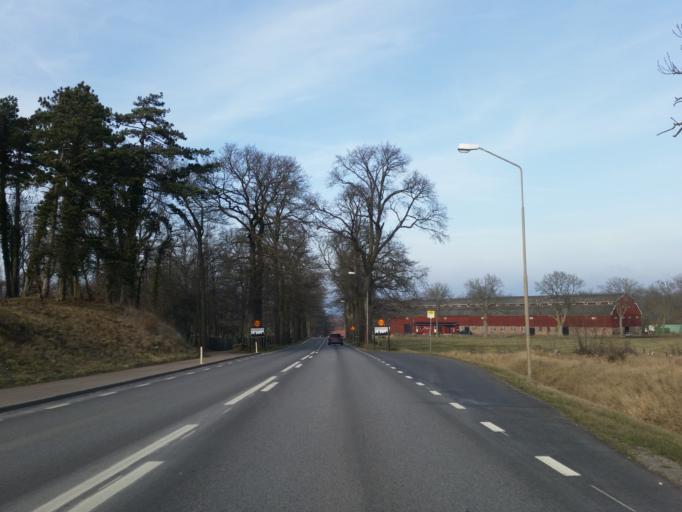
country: SE
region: Kalmar
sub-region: Borgholms Kommun
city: Borgholm
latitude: 56.8684
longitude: 16.6583
